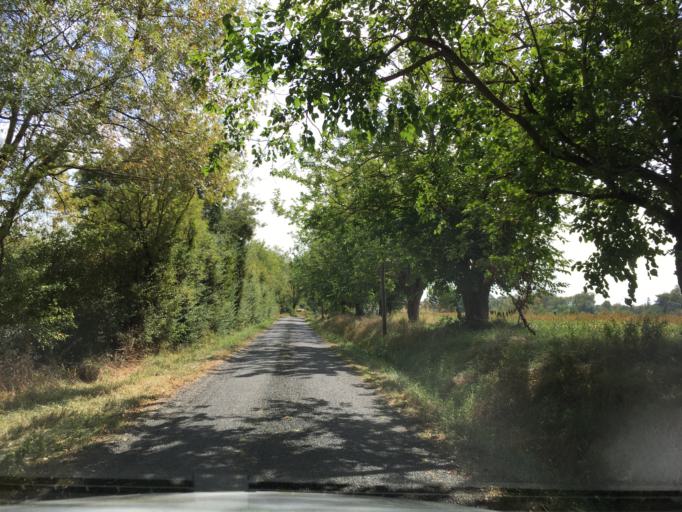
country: FR
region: Midi-Pyrenees
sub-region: Departement du Tarn
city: Castres
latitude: 43.6161
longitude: 2.2221
